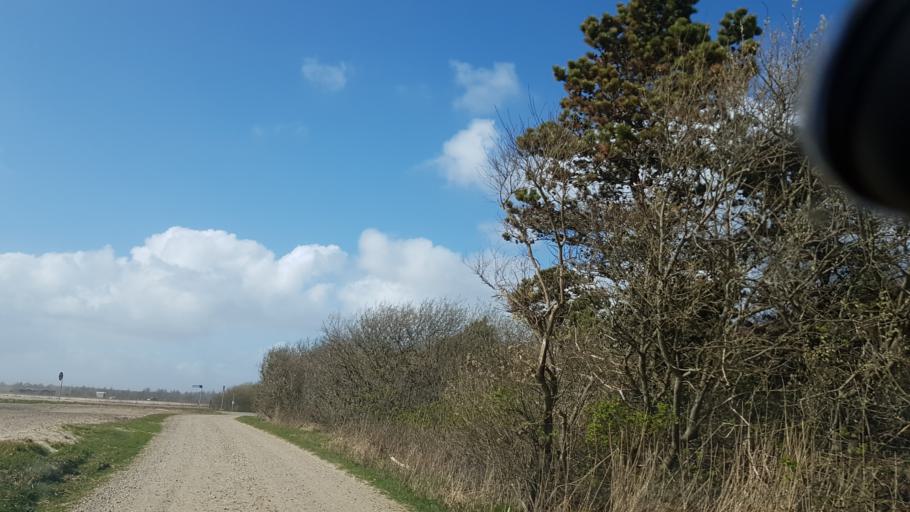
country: DE
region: Schleswig-Holstein
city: List
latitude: 55.0845
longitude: 8.5292
